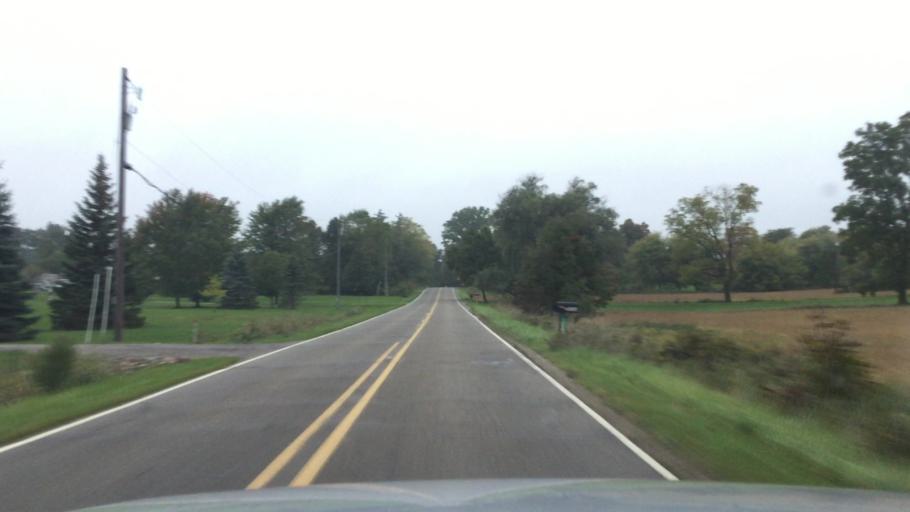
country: US
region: Michigan
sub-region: Shiawassee County
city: Corunna
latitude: 42.9378
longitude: -84.1395
